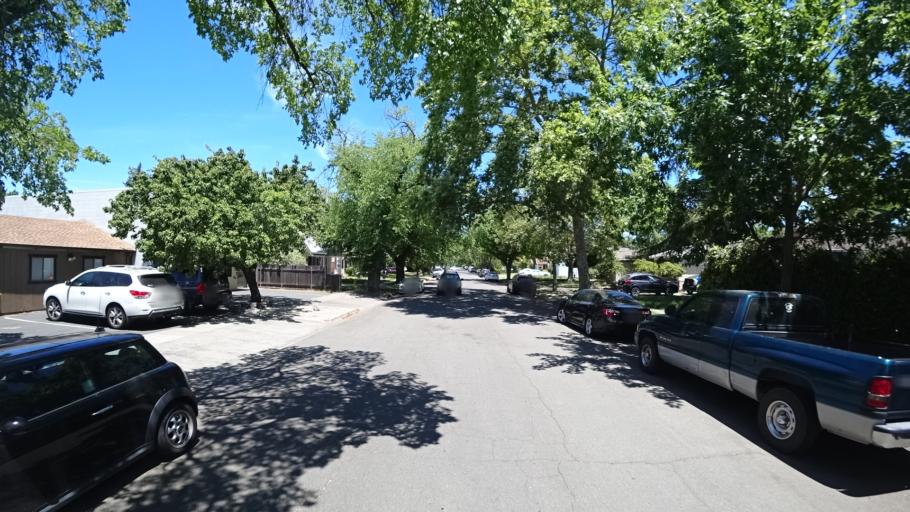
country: US
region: California
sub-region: Sacramento County
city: Sacramento
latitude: 38.5624
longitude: -121.4616
